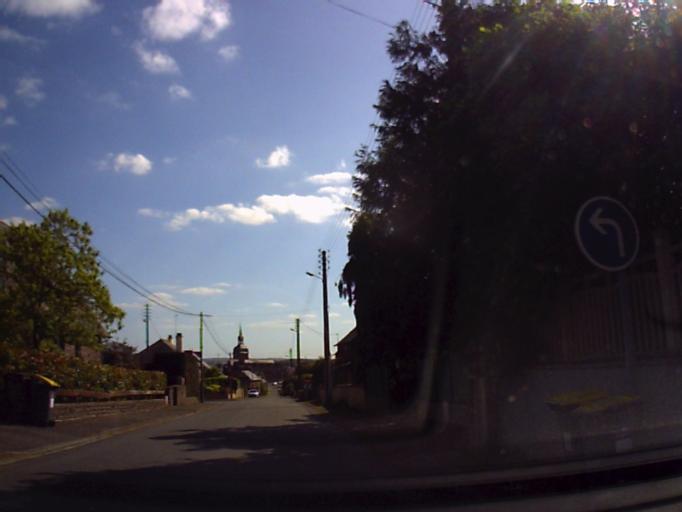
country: FR
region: Brittany
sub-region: Departement d'Ille-et-Vilaine
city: Iffendic
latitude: 48.1319
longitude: -2.0316
